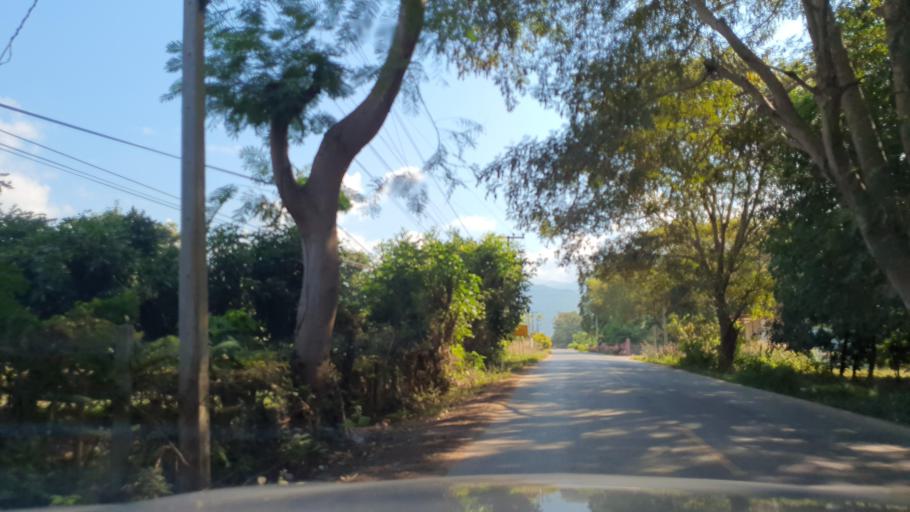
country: TH
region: Nan
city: Pua
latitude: 19.1411
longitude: 100.9277
